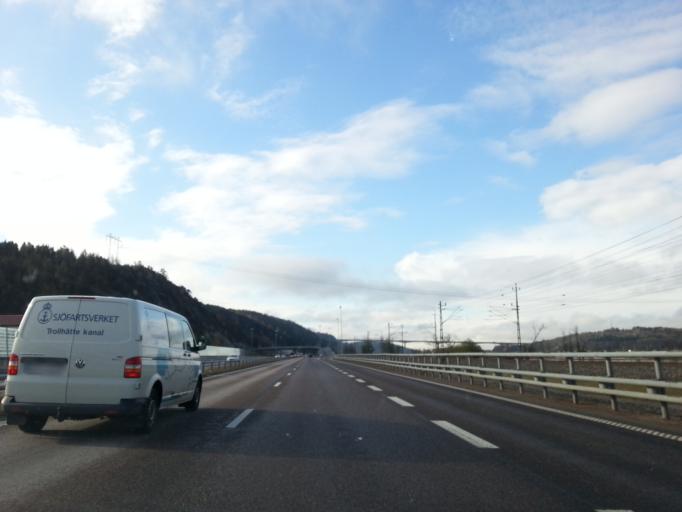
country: SE
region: Vaestra Goetaland
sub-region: Ale Kommun
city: Surte
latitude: 57.8199
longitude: 12.0151
